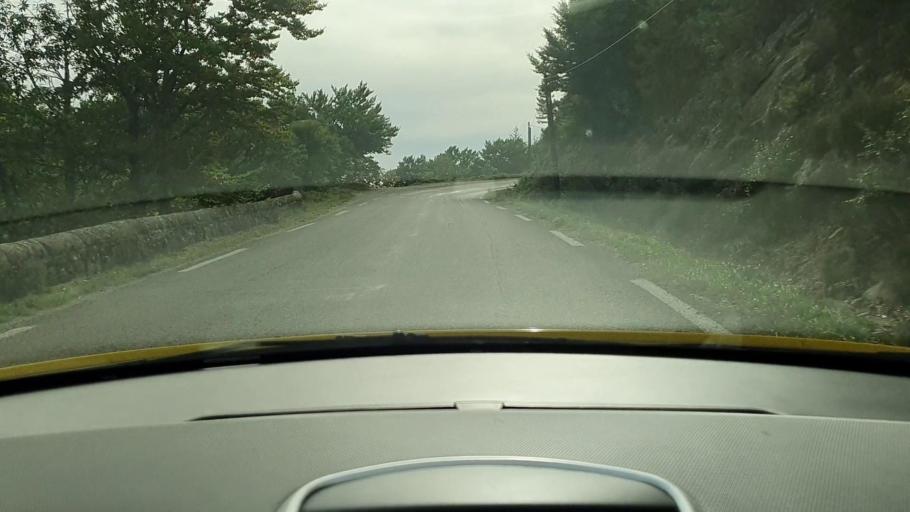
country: FR
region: Languedoc-Roussillon
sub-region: Departement du Gard
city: Le Vigan
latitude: 44.0244
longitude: 3.5817
